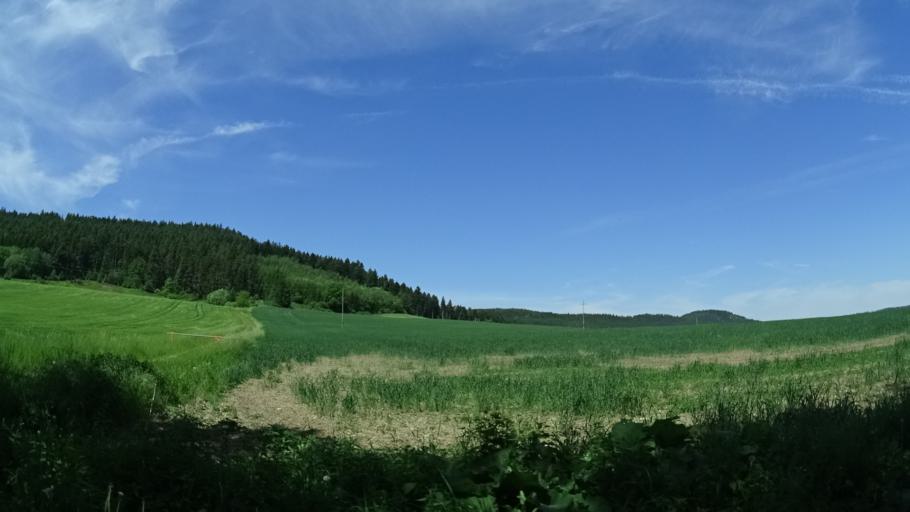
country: DE
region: Thuringia
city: Plaue
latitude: 50.7466
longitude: 10.9426
